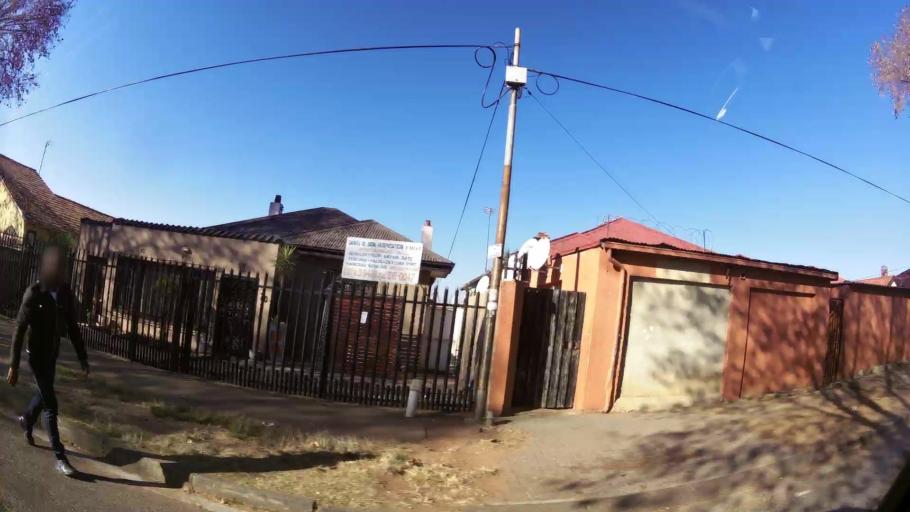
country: ZA
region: Gauteng
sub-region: City of Johannesburg Metropolitan Municipality
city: Johannesburg
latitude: -26.2026
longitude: 28.0976
